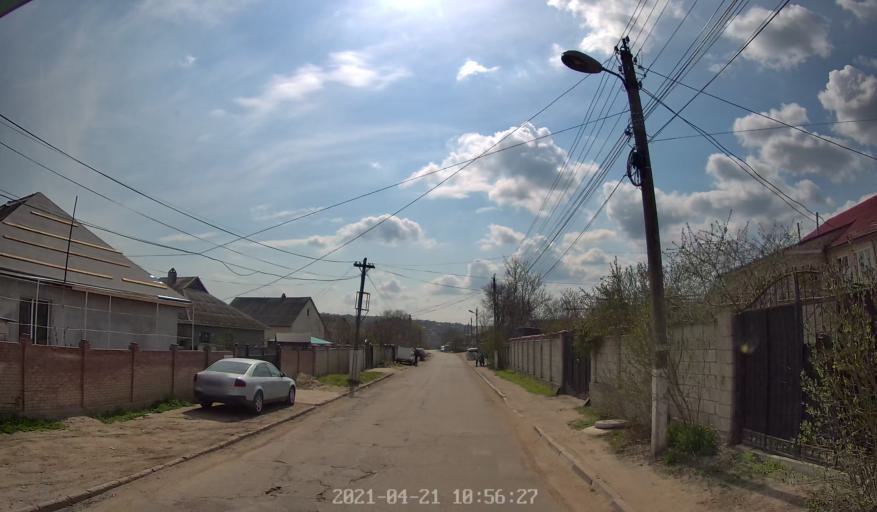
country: MD
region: Chisinau
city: Singera
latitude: 46.9647
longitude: 28.9343
